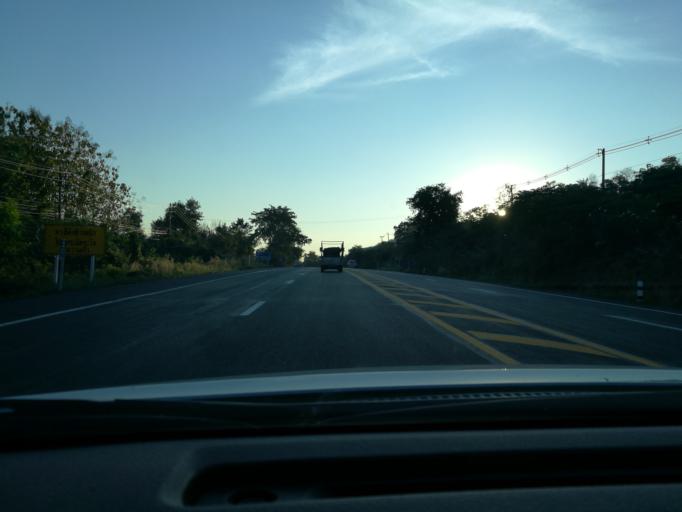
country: TH
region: Phitsanulok
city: Wang Thong
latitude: 16.8630
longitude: 100.4827
